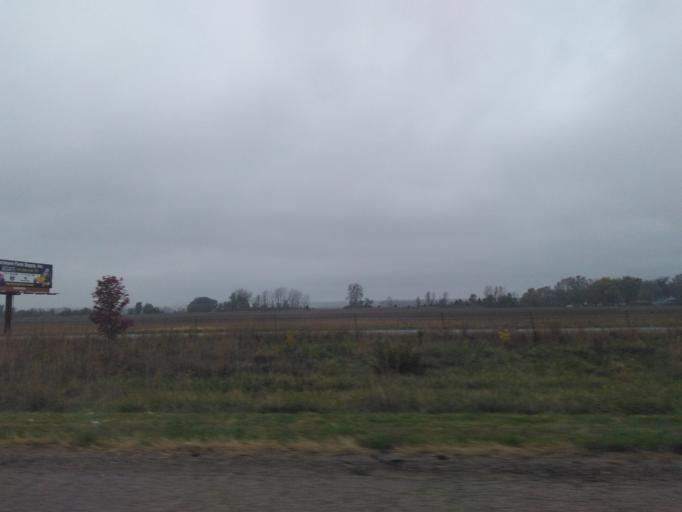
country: US
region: Illinois
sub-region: Saint Clair County
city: Dupo
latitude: 38.4882
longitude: -90.2192
